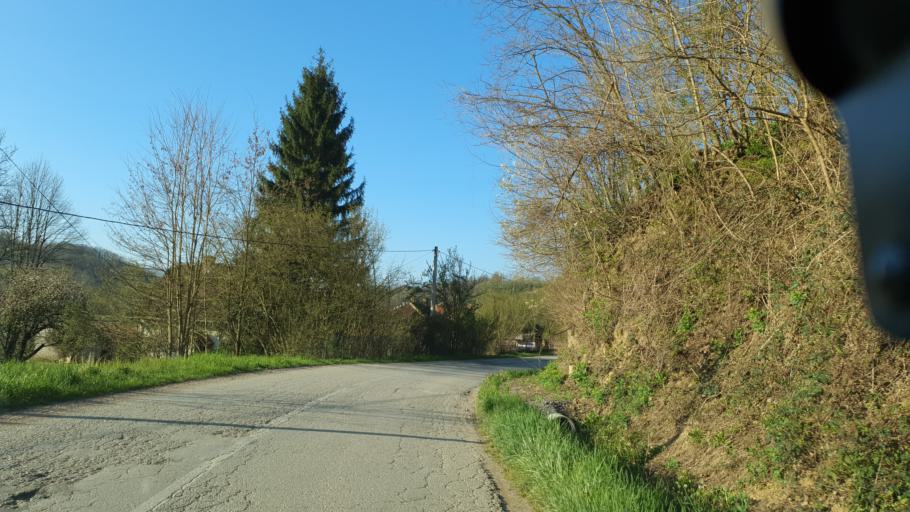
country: RS
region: Central Serbia
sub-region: Kolubarski Okrug
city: Osecina
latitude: 44.3497
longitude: 19.5200
